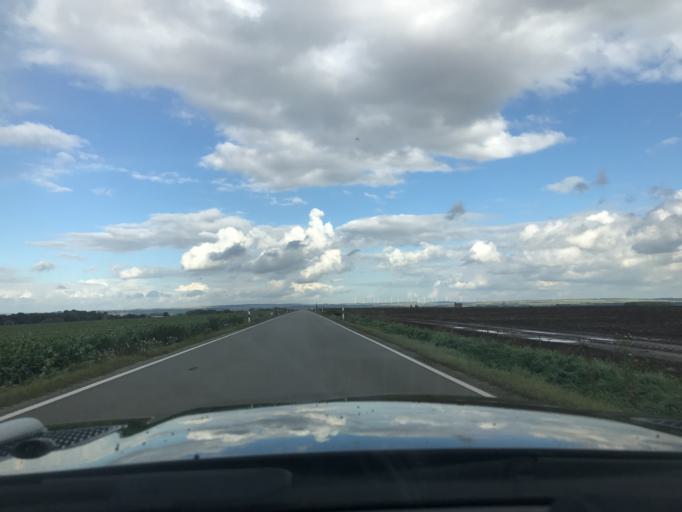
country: DE
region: Thuringia
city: Heroldishausen
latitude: 51.1360
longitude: 10.5324
